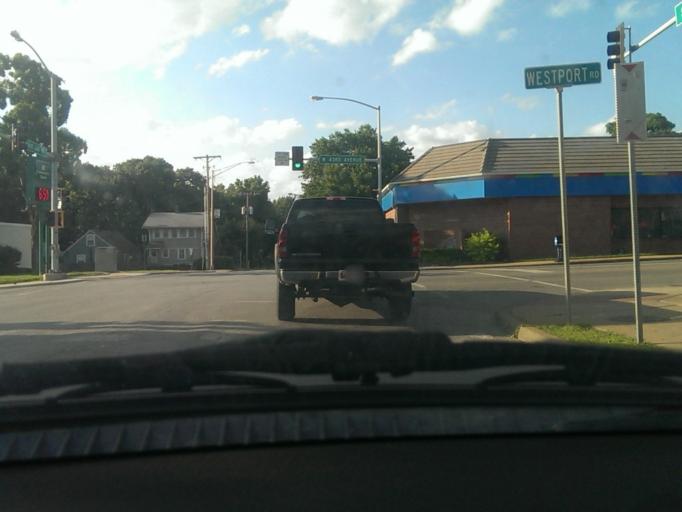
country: US
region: Kansas
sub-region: Johnson County
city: Westwood
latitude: 39.0500
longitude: -94.6073
